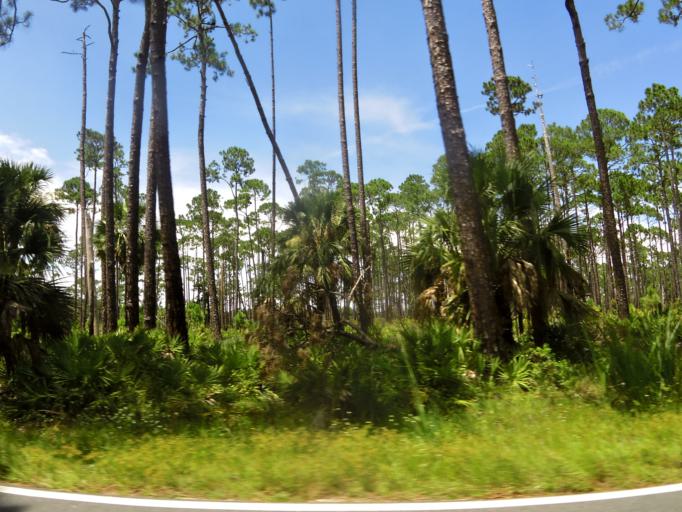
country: US
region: Florida
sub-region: Volusia County
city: Ormond-by-the-Sea
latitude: 29.3566
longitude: -81.1126
